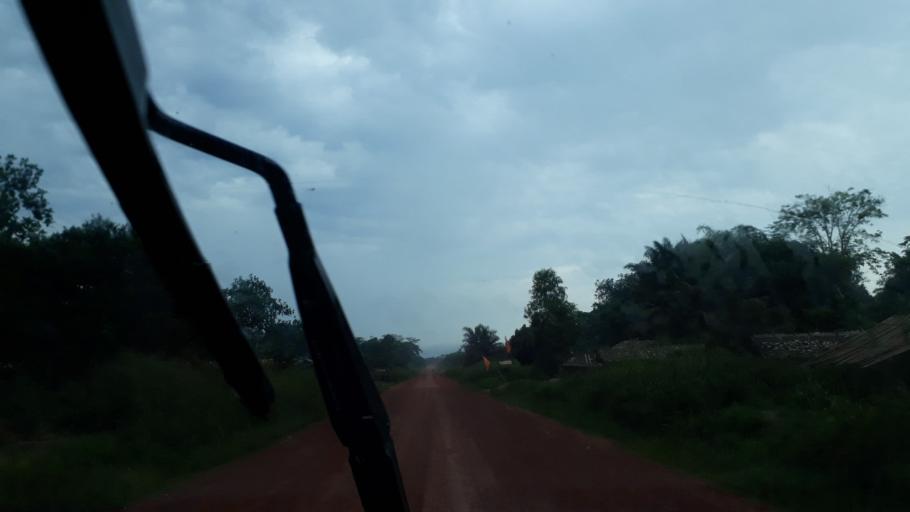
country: CD
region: Eastern Province
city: Kisangani
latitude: 0.4689
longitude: 25.3857
